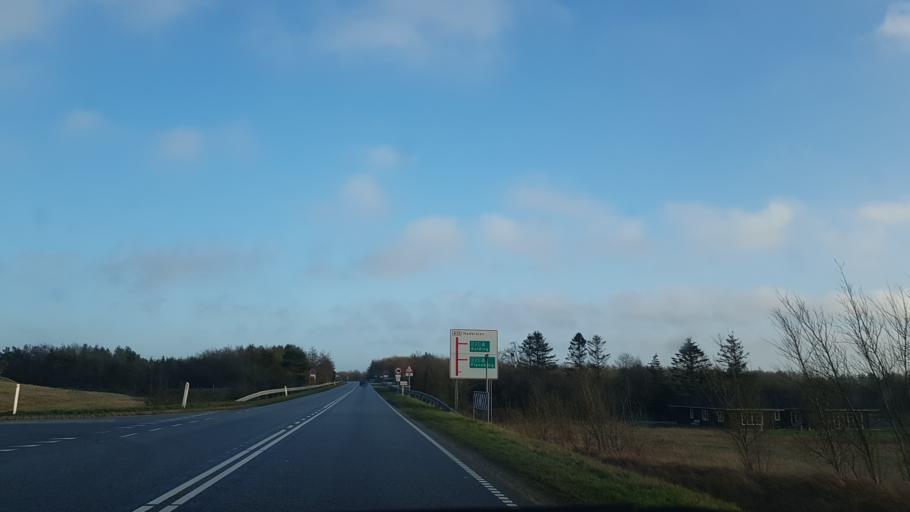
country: DK
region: South Denmark
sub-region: Haderslev Kommune
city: Vojens
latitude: 55.1714
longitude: 9.3692
